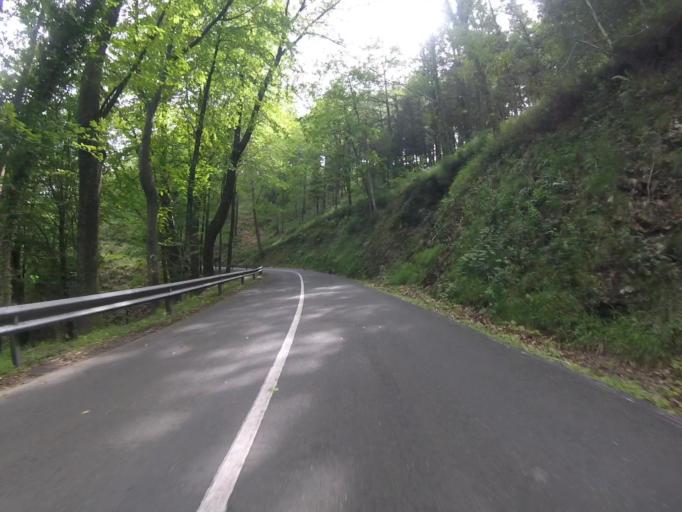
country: ES
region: Navarre
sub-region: Provincia de Navarra
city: Arano
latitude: 43.2557
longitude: -1.8496
